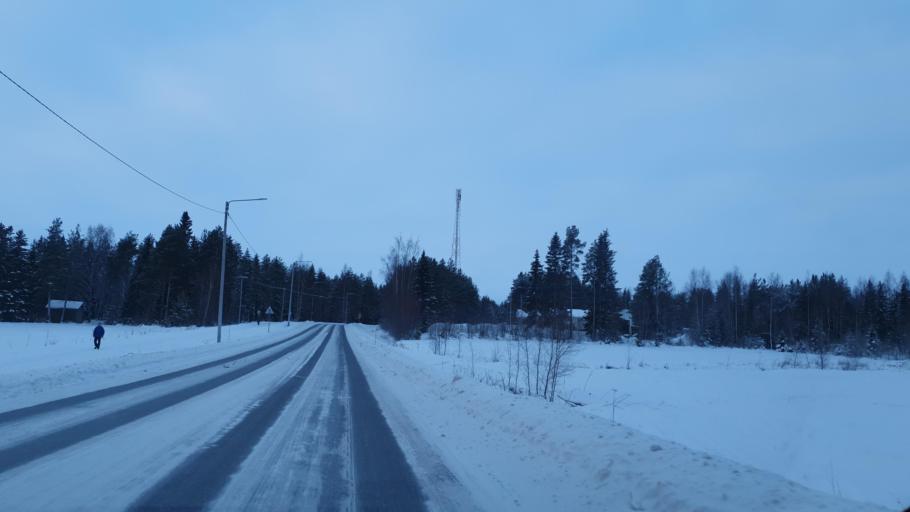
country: FI
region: Northern Ostrobothnia
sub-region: Oulu
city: Haukipudas
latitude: 65.2077
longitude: 25.3282
